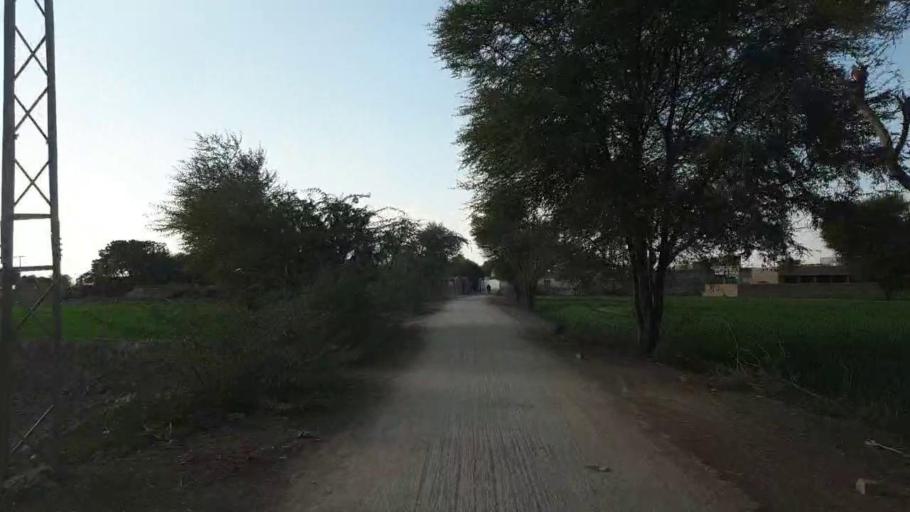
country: PK
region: Sindh
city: Shahpur Chakar
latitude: 26.1305
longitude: 68.5596
